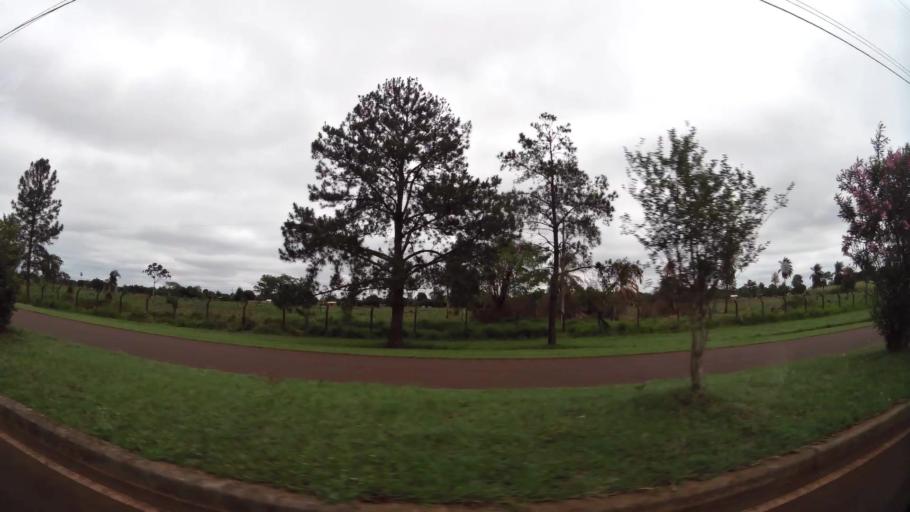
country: PY
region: Alto Parana
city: Colonia Yguazu
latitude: -25.4794
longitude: -54.8611
